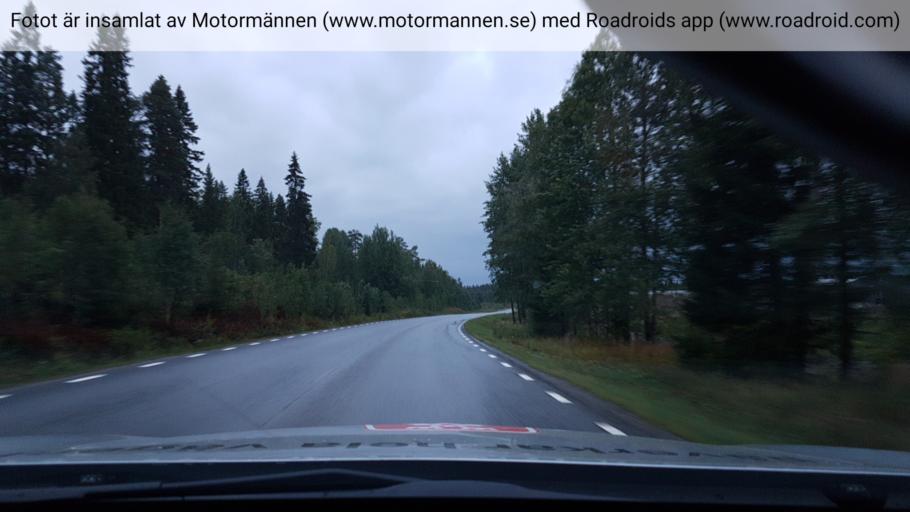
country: SE
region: Vaesterbotten
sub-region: Umea Kommun
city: Ersmark
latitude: 63.8662
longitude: 20.3004
